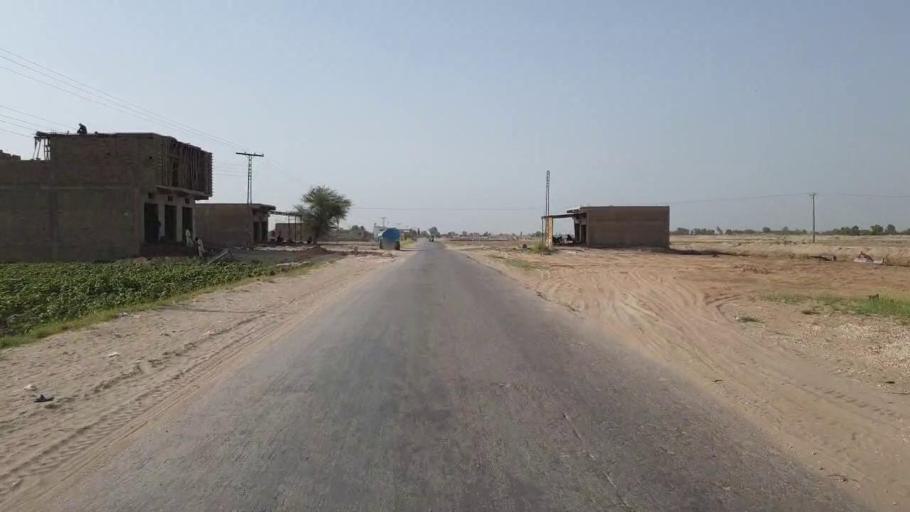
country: PK
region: Sindh
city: Sanghar
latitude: 26.2808
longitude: 68.9304
